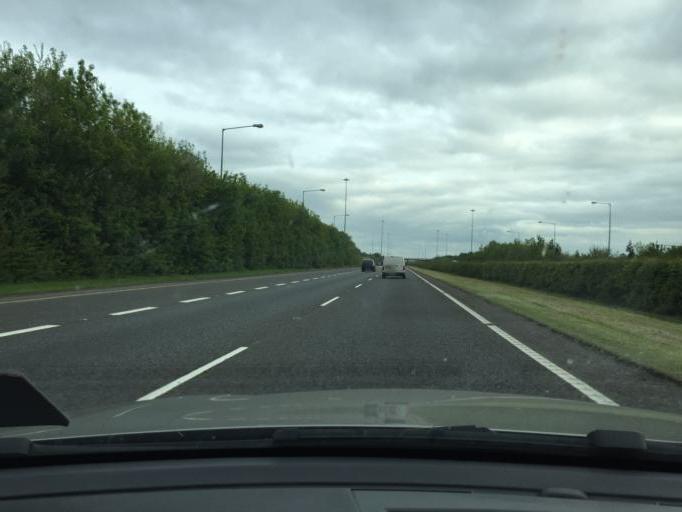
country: IE
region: Leinster
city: Balrothery
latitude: 53.5698
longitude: -6.2121
